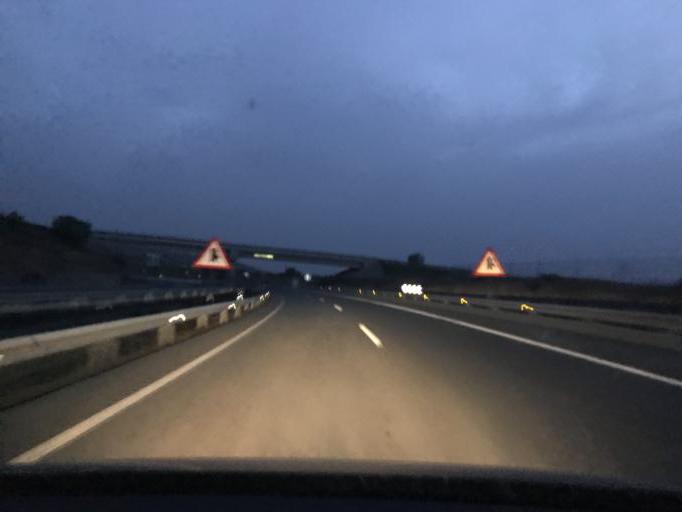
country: ES
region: Andalusia
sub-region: Provincia de Granada
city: Gor
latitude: 37.3988
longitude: -2.9906
